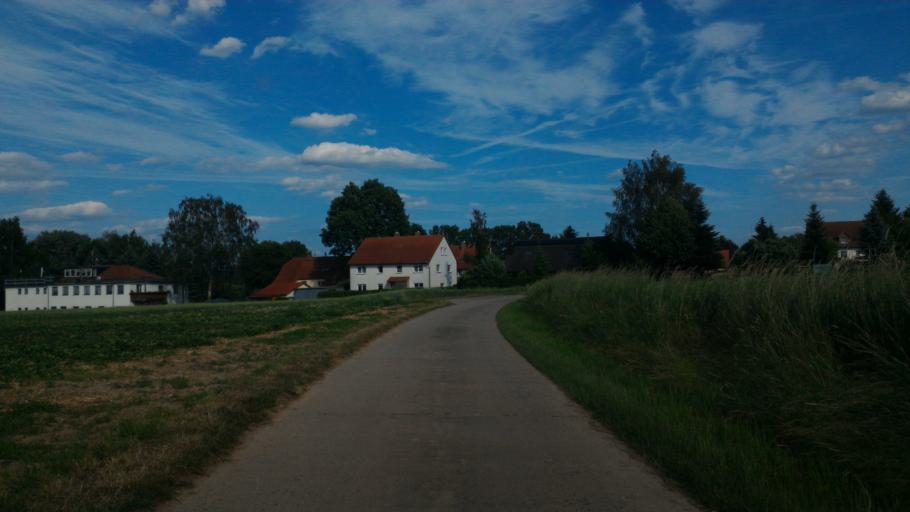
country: DE
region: Saxony
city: Zittau
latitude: 50.8664
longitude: 14.8006
